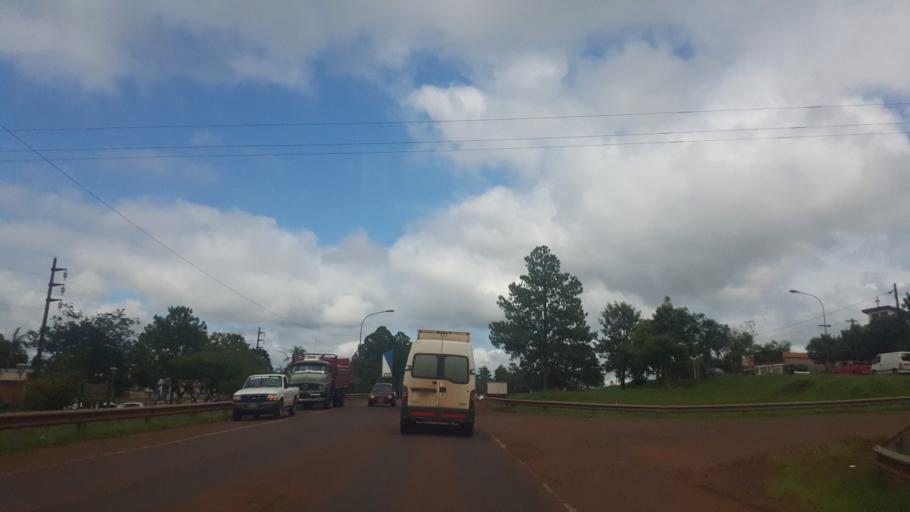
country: AR
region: Misiones
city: Aristobulo del Valle
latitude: -27.0849
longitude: -54.8306
